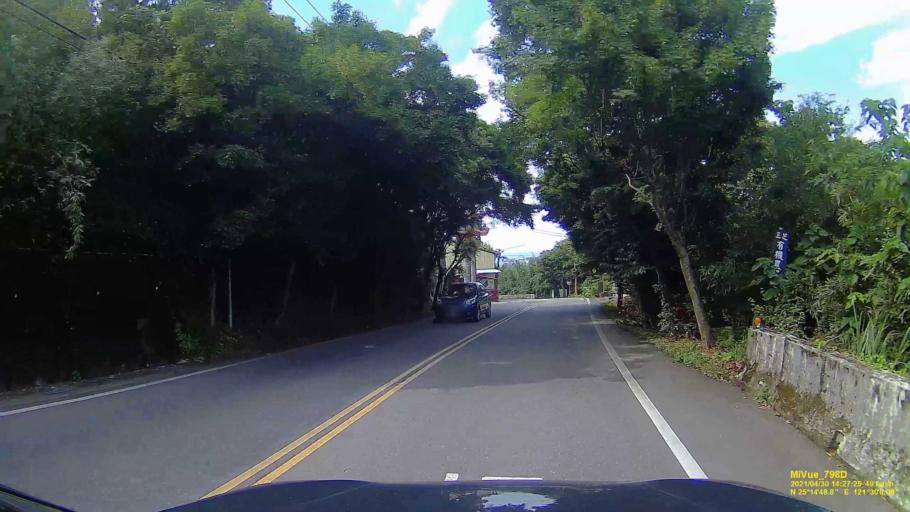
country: TW
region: Taipei
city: Taipei
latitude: 25.2472
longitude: 121.5017
